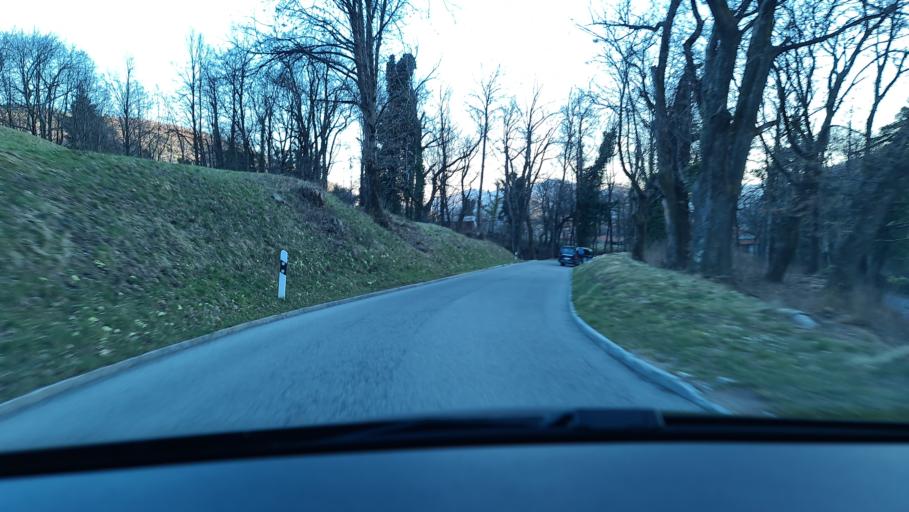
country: CH
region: Ticino
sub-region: Lugano District
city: Pura
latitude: 46.0335
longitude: 8.8662
